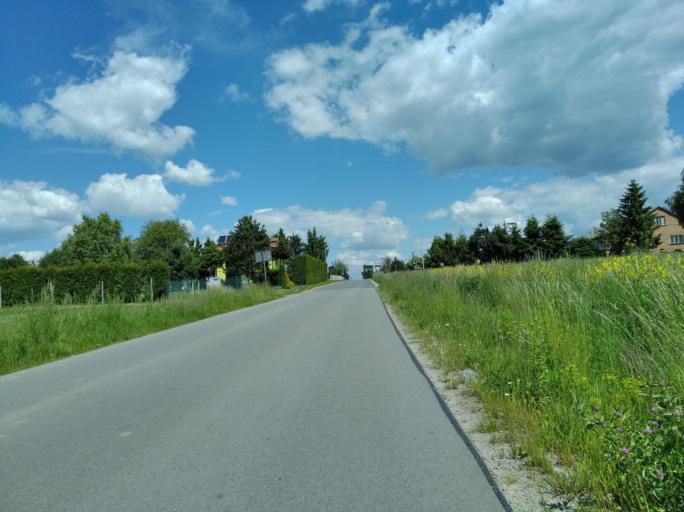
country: PL
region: Subcarpathian Voivodeship
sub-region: Powiat jasielski
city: Tarnowiec
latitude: 49.7749
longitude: 21.6113
